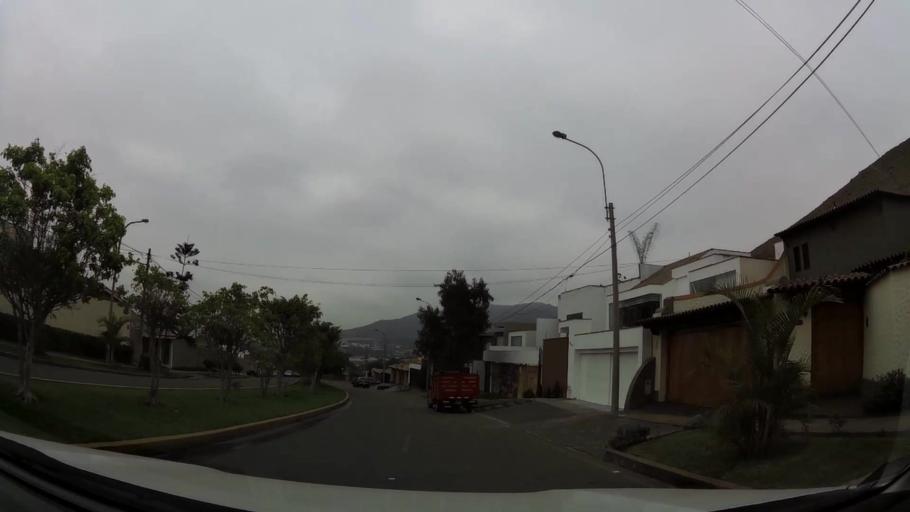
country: PE
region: Lima
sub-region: Lima
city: La Molina
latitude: -12.0937
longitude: -76.9227
